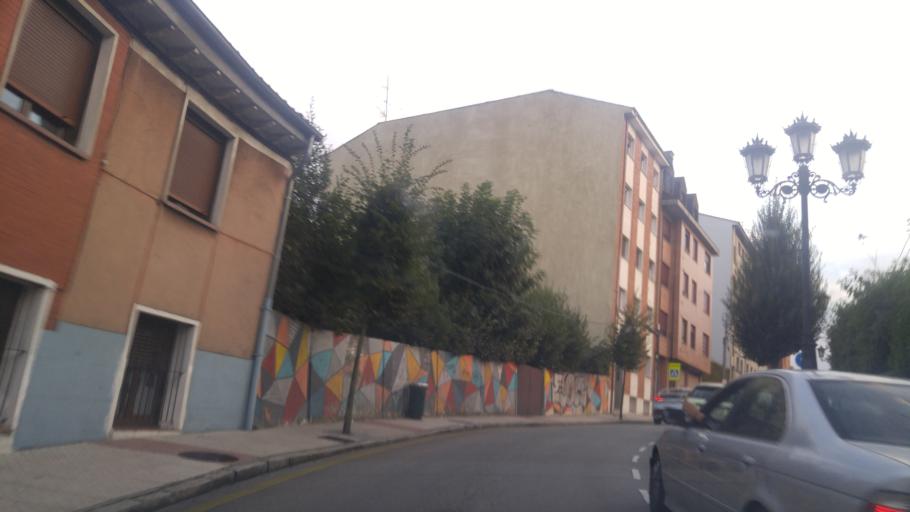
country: ES
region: Asturias
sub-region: Province of Asturias
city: Oviedo
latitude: 43.3723
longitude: -5.8571
